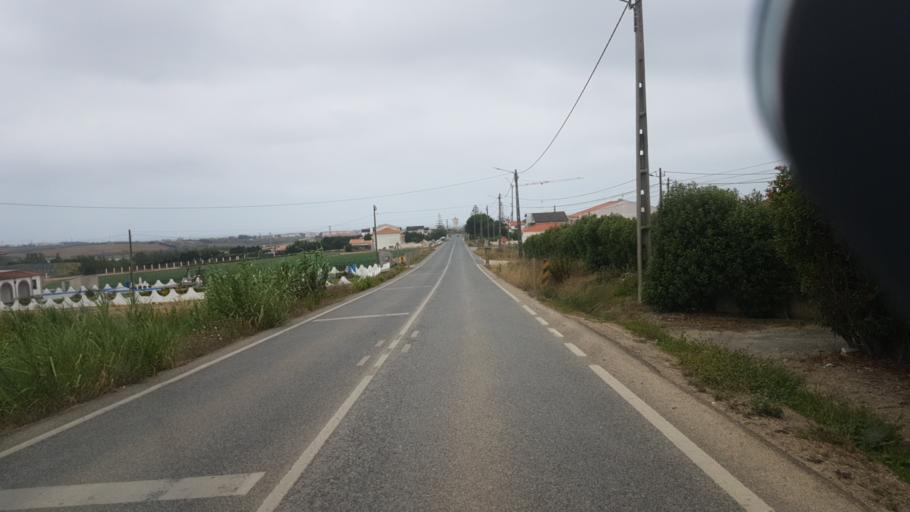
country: PT
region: Leiria
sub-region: Peniche
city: Atouguia da Baleia
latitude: 39.3355
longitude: -9.3005
